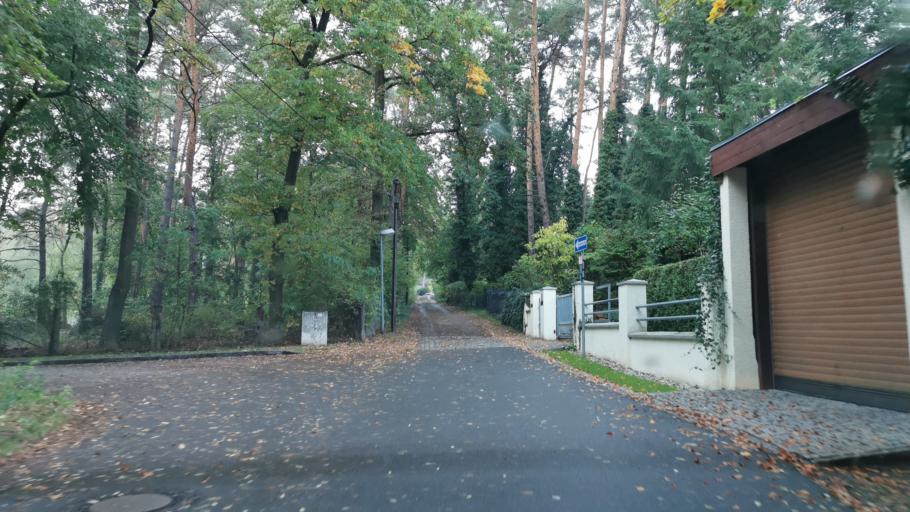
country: DE
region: Brandenburg
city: Michendorf
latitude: 52.3331
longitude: 13.0598
